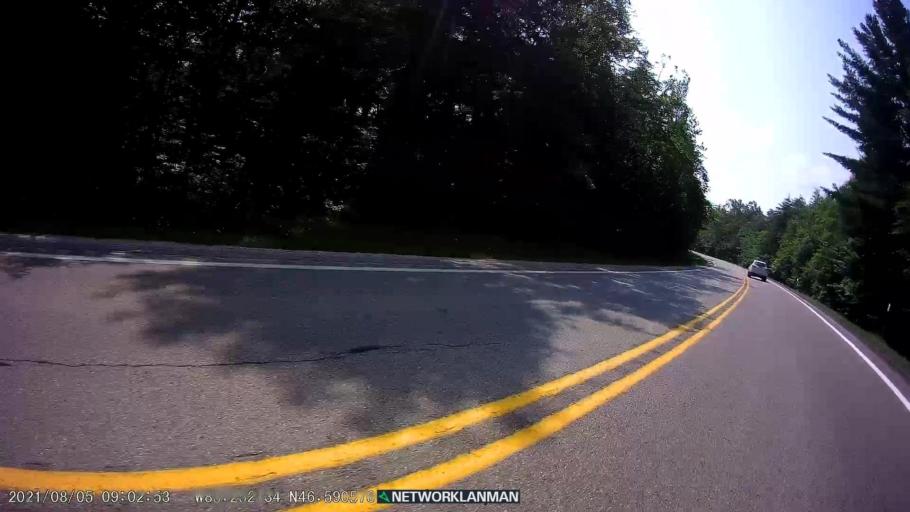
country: US
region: Michigan
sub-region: Luce County
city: Newberry
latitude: 46.5901
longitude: -85.2527
